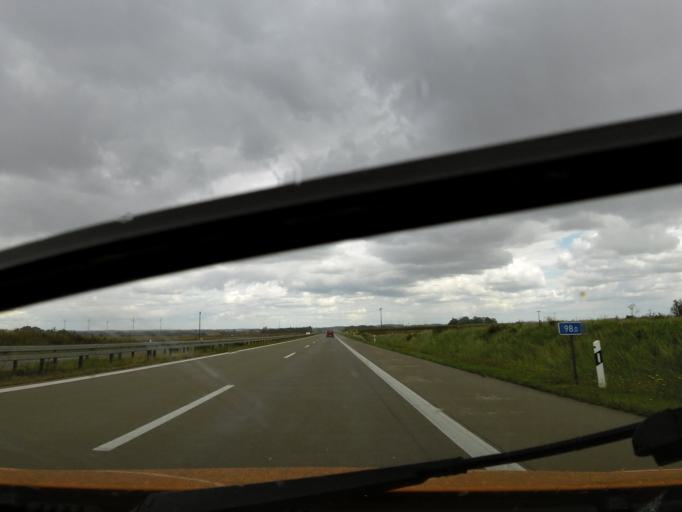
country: DE
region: Mecklenburg-Vorpommern
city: Penkun
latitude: 53.3088
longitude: 14.2347
